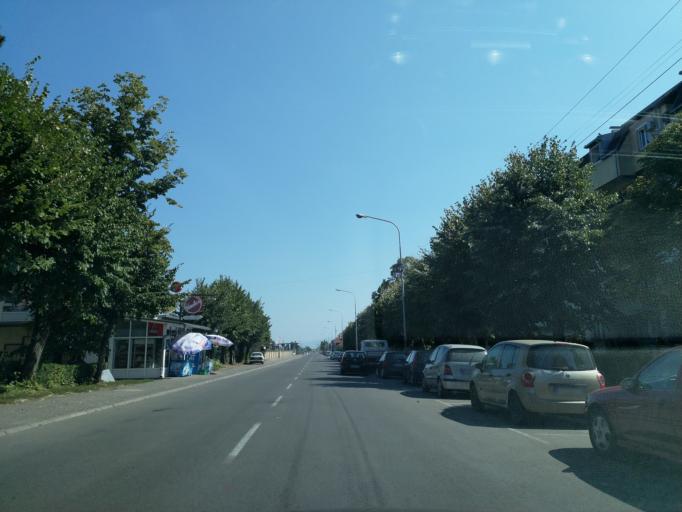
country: RS
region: Central Serbia
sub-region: Rasinski Okrug
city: Trstenik
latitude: 43.6169
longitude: 21.0091
